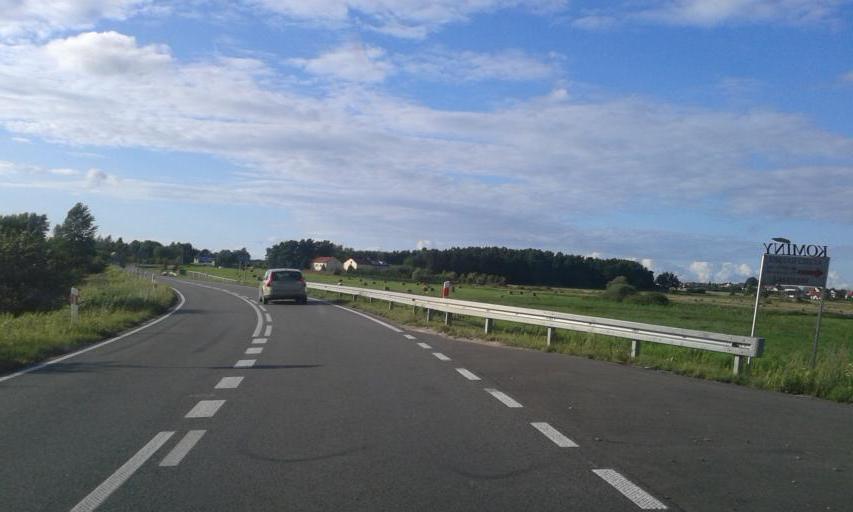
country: PL
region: West Pomeranian Voivodeship
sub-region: Koszalin
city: Koszalin
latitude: 54.1350
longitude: 16.1721
